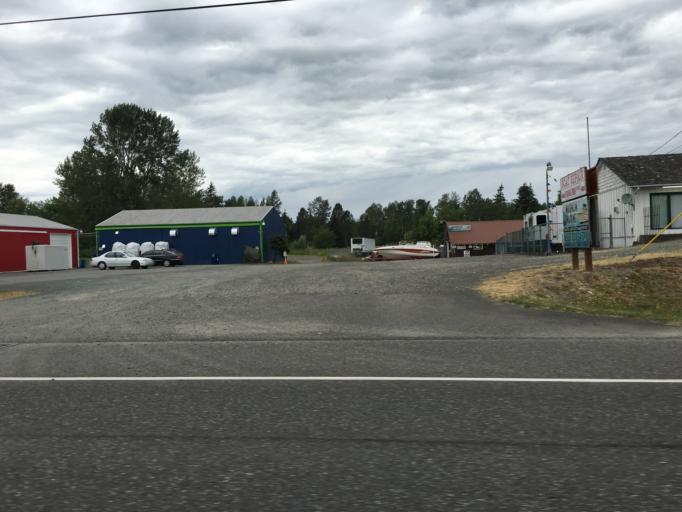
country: US
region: Washington
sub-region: Whatcom County
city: Bellingham
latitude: 48.8195
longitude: -122.4861
